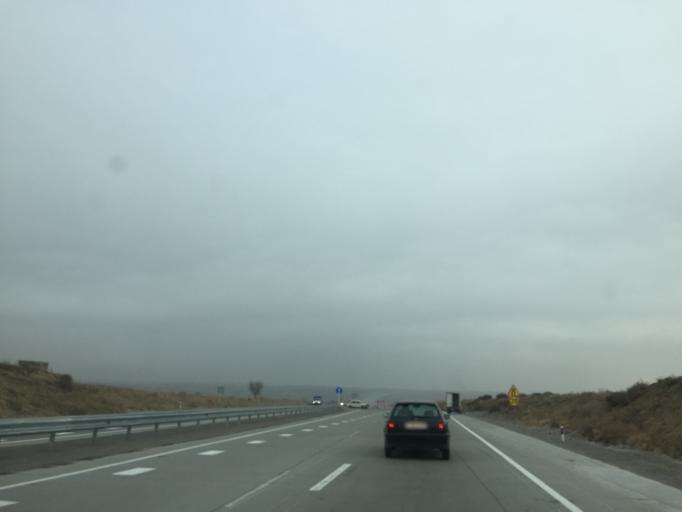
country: KZ
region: Ongtustik Qazaqstan
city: Aksu
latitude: 42.4520
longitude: 69.7487
